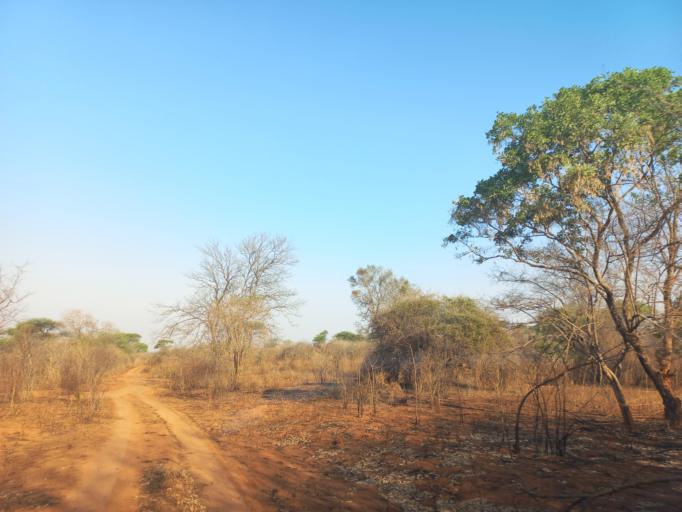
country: ZM
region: Lusaka
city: Luangwa
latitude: -15.4189
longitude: 30.2569
